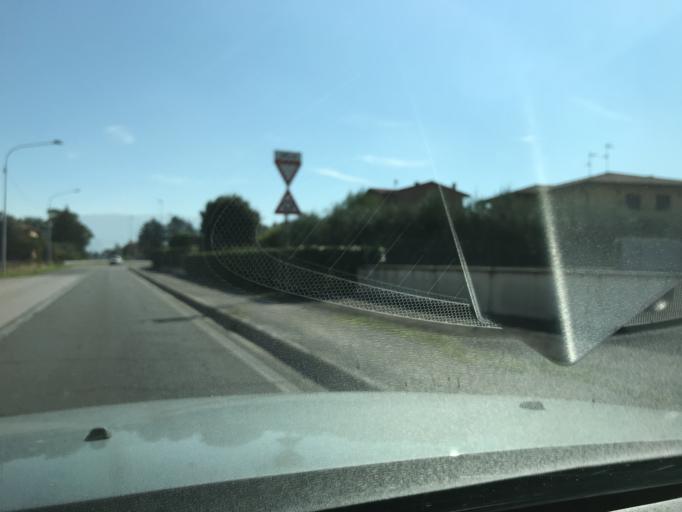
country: IT
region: Umbria
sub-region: Provincia di Perugia
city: Ospedalicchio
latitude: 43.0790
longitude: 12.5075
